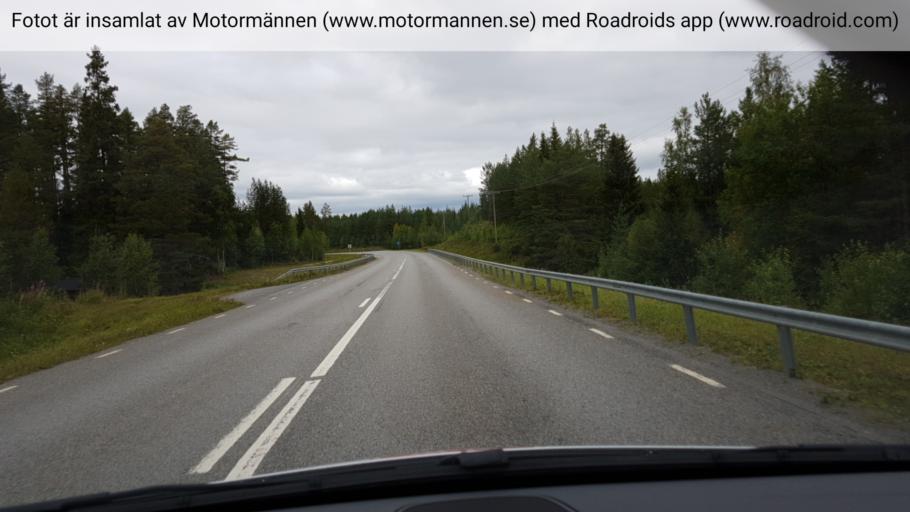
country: SE
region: Jaemtland
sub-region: Stroemsunds Kommun
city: Stroemsund
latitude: 64.2444
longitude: 15.4496
